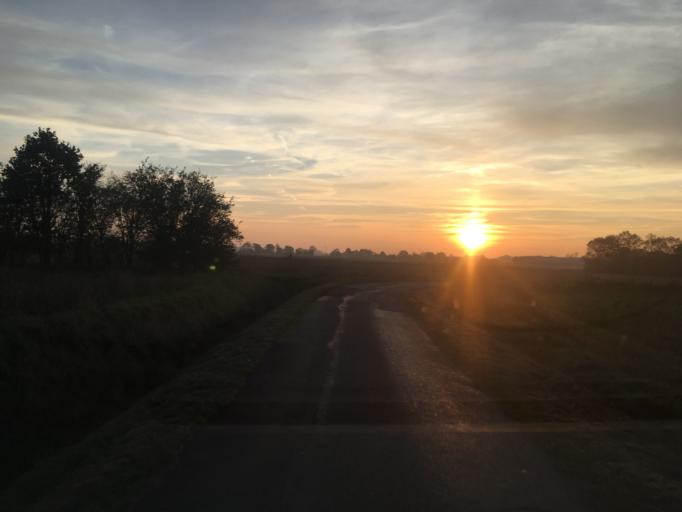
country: DE
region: Schleswig-Holstein
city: Bramstedtlund
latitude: 54.9843
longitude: 9.0842
